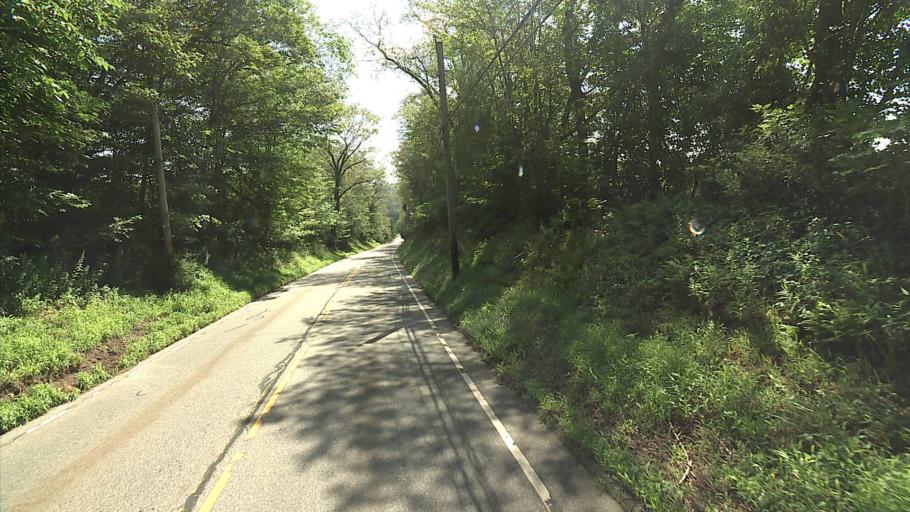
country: US
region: Connecticut
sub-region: Windham County
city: Windham
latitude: 41.6975
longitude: -72.1172
